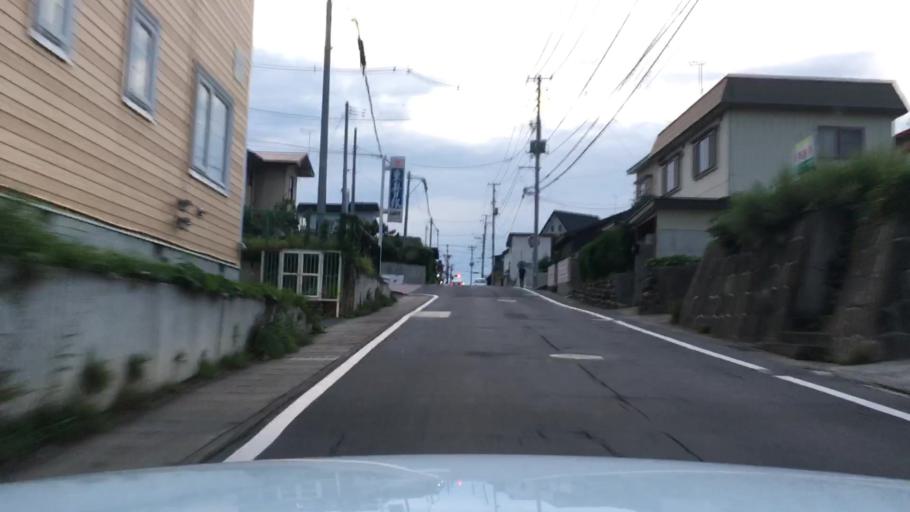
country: JP
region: Aomori
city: Hirosaki
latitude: 40.5927
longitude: 140.4669
